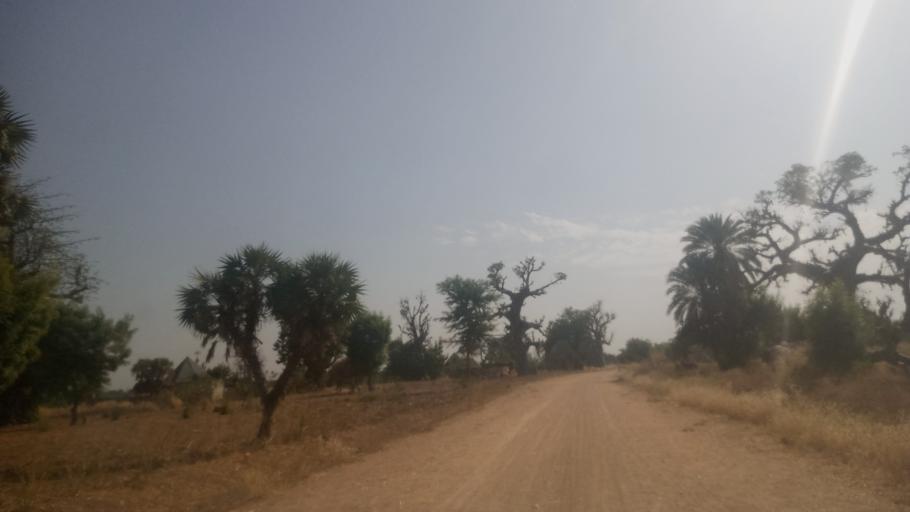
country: NG
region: Adamawa
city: Mayo Belwa
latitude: 9.0751
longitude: 12.0351
